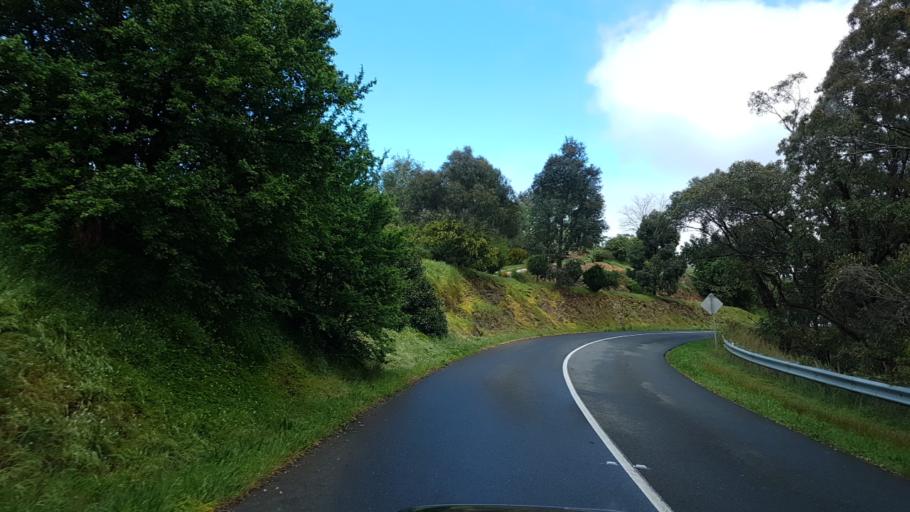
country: AU
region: South Australia
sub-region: Adelaide Hills
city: Adelaide Hills
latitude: -34.9102
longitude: 138.7608
